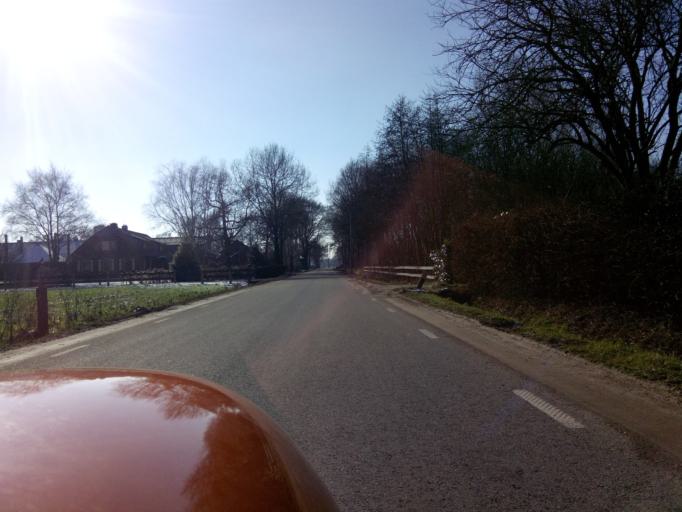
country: NL
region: Gelderland
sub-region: Gemeente Barneveld
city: Kootwijkerbroek
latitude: 52.1676
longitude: 5.6414
